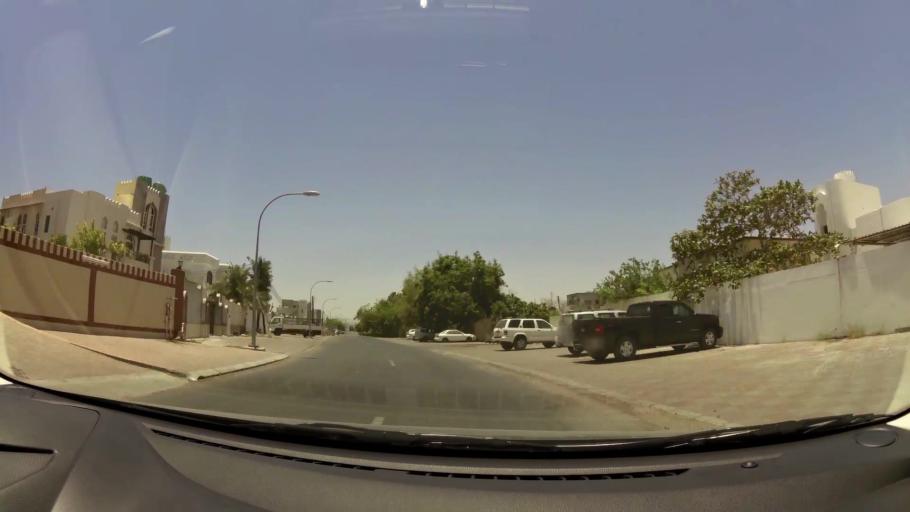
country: OM
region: Muhafazat Masqat
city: As Sib al Jadidah
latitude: 23.6354
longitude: 58.2323
